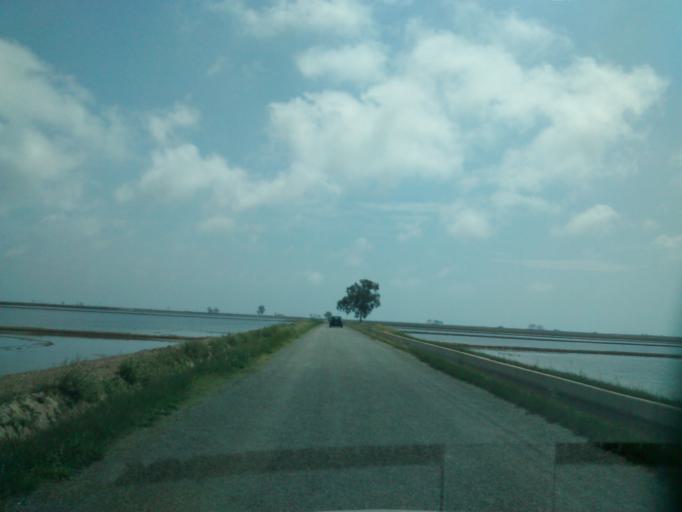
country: ES
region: Catalonia
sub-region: Provincia de Tarragona
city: Deltebre
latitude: 40.6881
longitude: 0.7828
